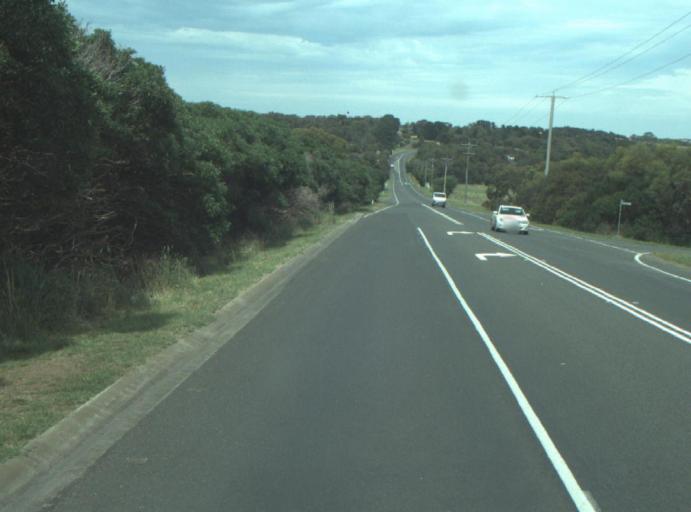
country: AU
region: Victoria
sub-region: Greater Geelong
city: Clifton Springs
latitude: -38.1540
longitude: 144.5896
